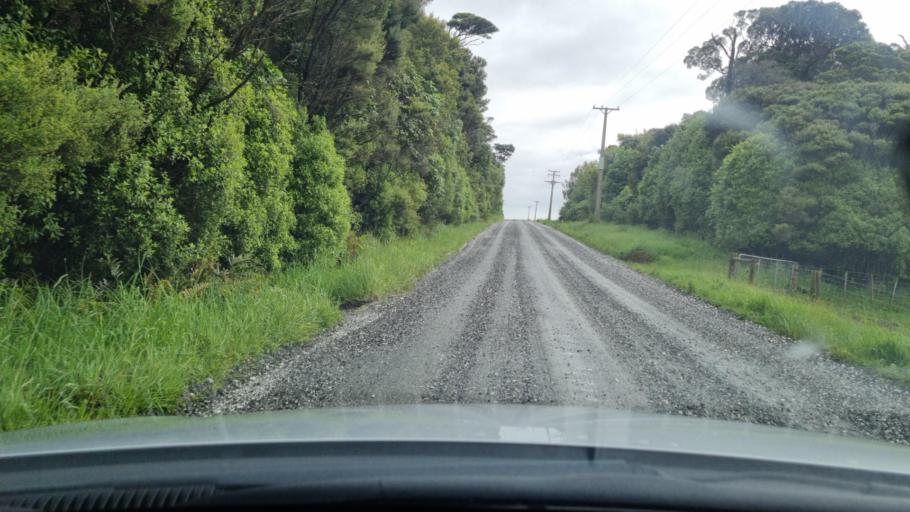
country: NZ
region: Southland
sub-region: Invercargill City
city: Bluff
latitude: -46.5284
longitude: 168.2691
